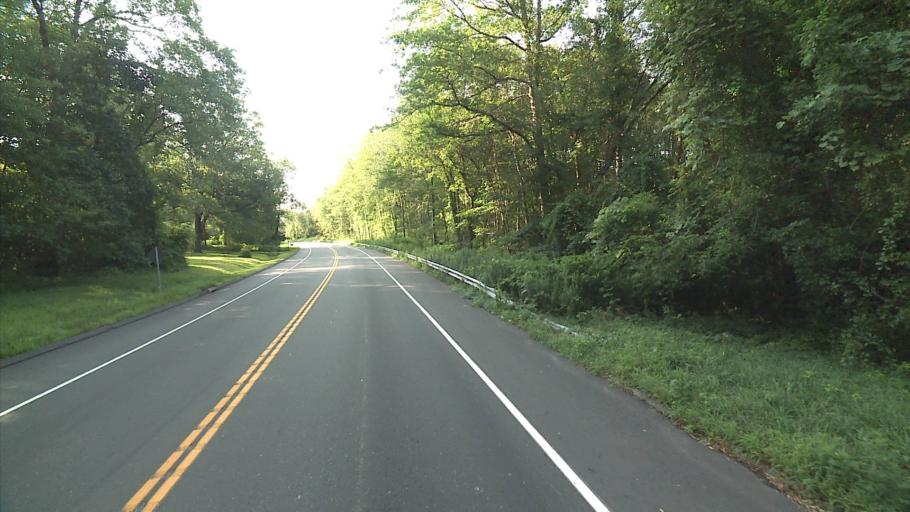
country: US
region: Connecticut
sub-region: New London County
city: Norwich
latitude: 41.4961
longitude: -72.0304
